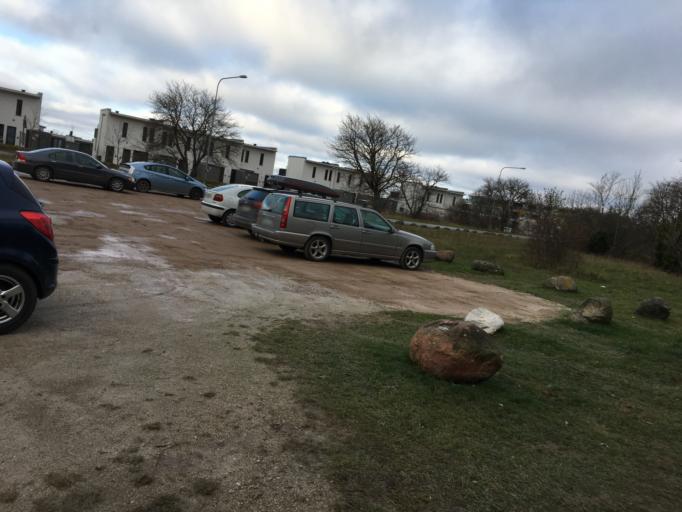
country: SE
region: Gotland
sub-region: Gotland
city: Visby
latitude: 57.6514
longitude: 18.3065
